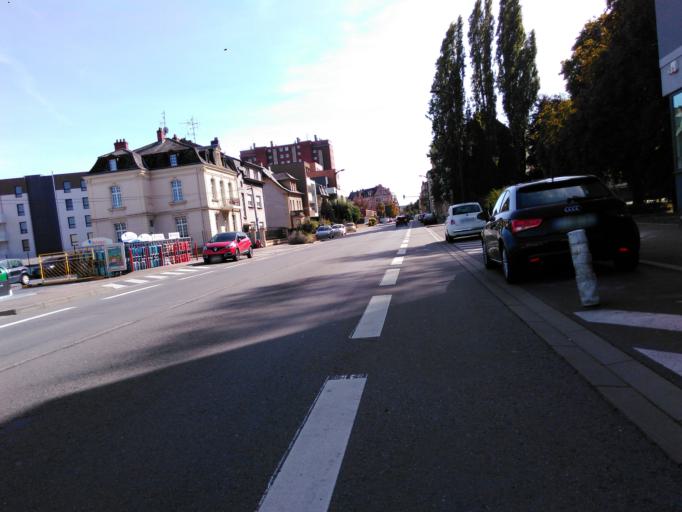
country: FR
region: Lorraine
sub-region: Departement de la Moselle
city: Thionville
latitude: 49.3649
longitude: 6.1687
